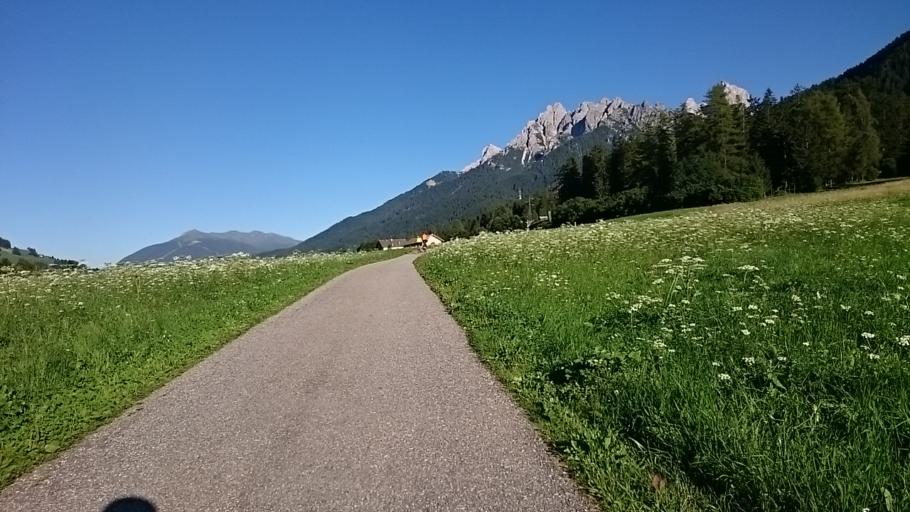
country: IT
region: Trentino-Alto Adige
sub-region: Bolzano
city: Villabassa
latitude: 46.7300
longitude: 12.1961
